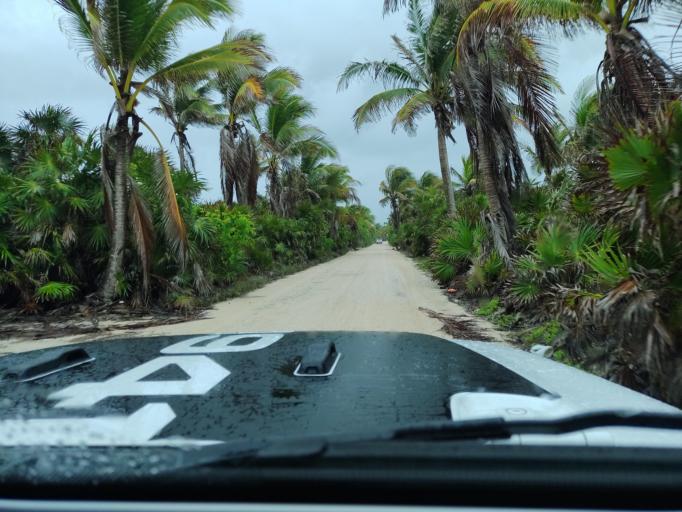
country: MX
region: Quintana Roo
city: Tulum
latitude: 19.9882
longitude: -87.4648
